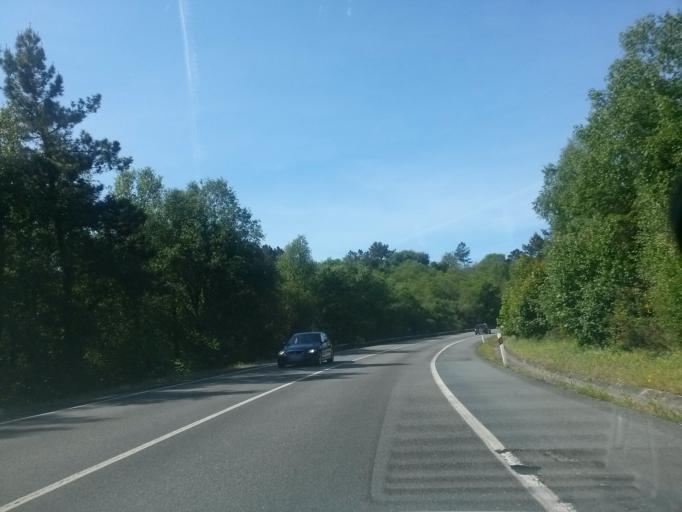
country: ES
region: Galicia
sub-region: Provincia de Lugo
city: Lugo
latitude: 43.0002
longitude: -7.5831
